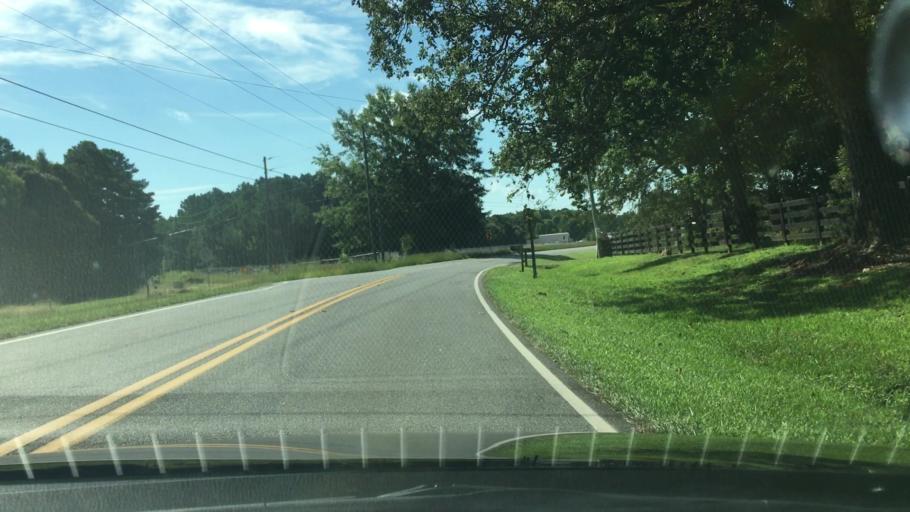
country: US
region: Georgia
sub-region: Putnam County
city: Jefferson
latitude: 33.4424
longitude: -83.2824
